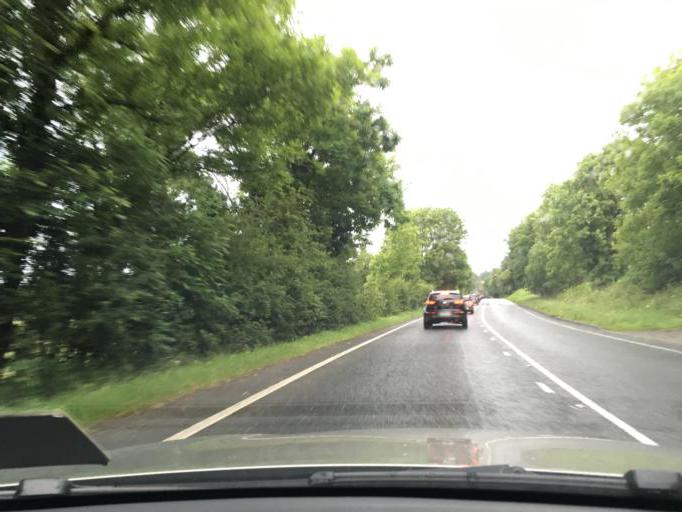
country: GB
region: Northern Ireland
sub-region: Fermanagh District
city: Enniskillen
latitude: 54.3800
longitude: -7.6370
